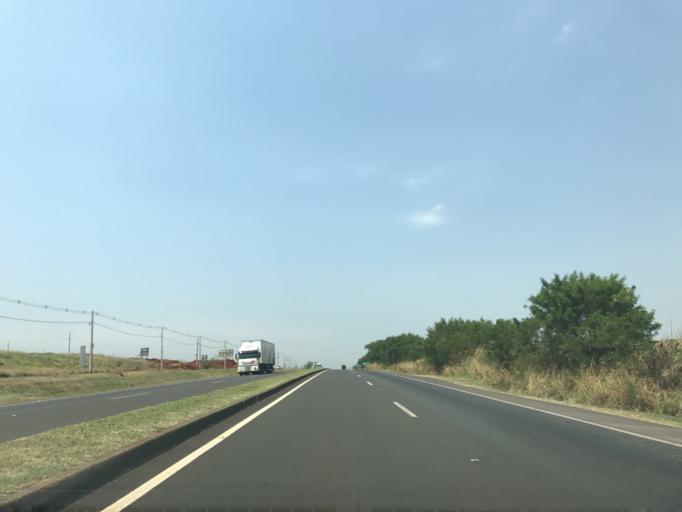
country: BR
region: Parana
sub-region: Marialva
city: Marialva
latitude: -23.4963
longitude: -51.8086
